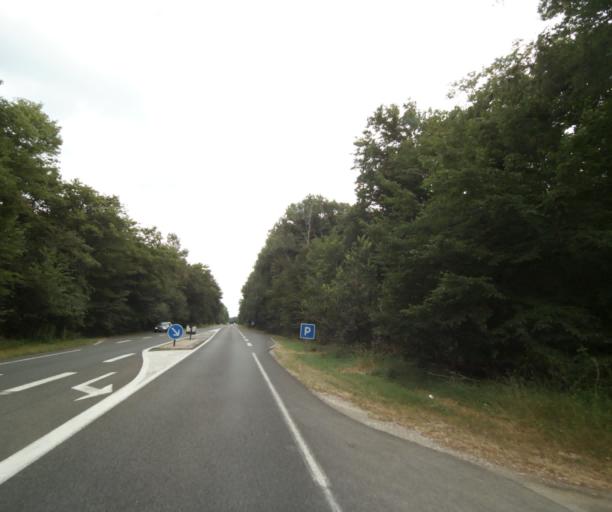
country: FR
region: Ile-de-France
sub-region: Departement de Seine-et-Marne
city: Bois-le-Roi
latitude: 48.4605
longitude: 2.6829
